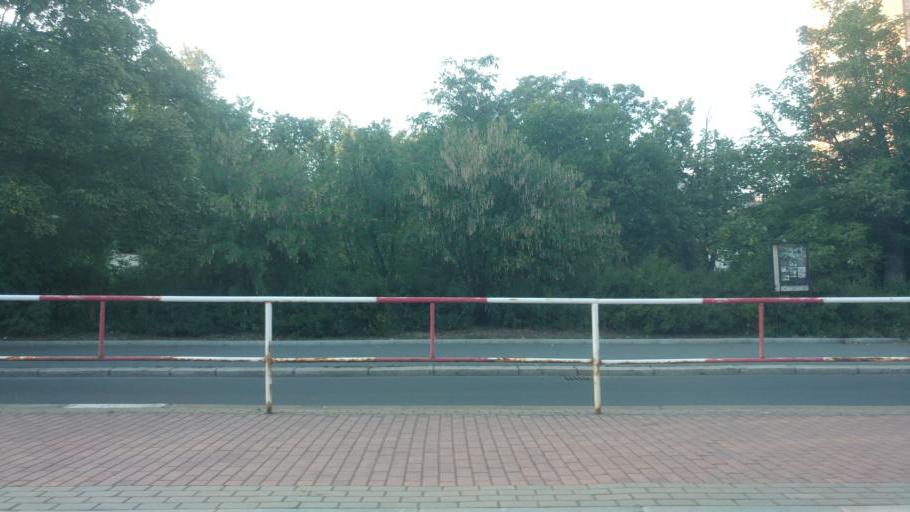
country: CZ
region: Praha
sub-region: Praha 8
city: Liben
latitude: 50.0772
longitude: 14.4855
